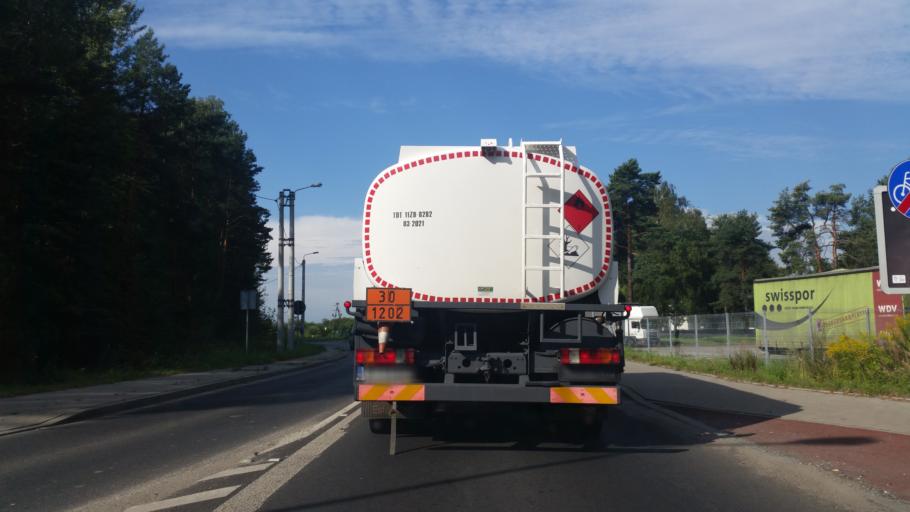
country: PL
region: Lesser Poland Voivodeship
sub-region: Powiat chrzanowski
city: Chrzanow
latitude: 50.1305
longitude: 19.3717
